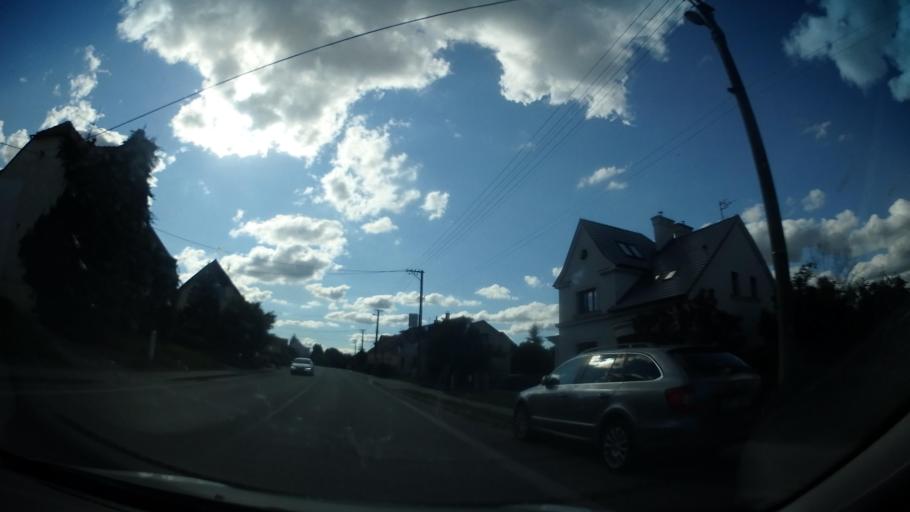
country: CZ
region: South Moravian
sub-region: Okres Blansko
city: Rajec-Jestrebi
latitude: 49.4095
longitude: 16.6215
